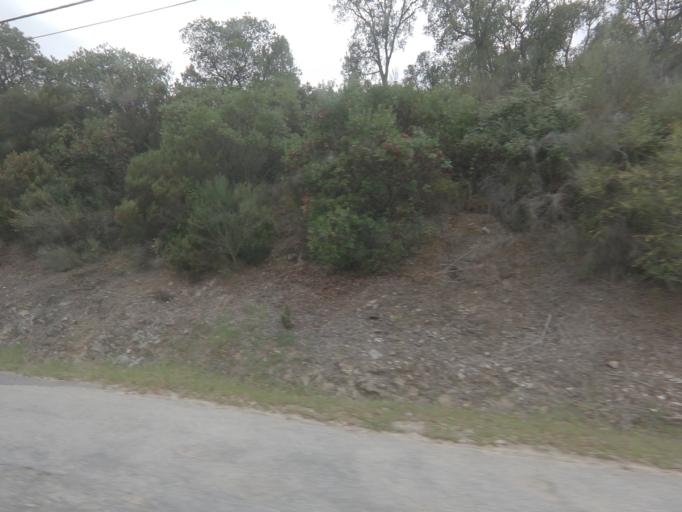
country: PT
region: Viseu
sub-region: Armamar
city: Armamar
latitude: 41.1281
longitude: -7.6432
